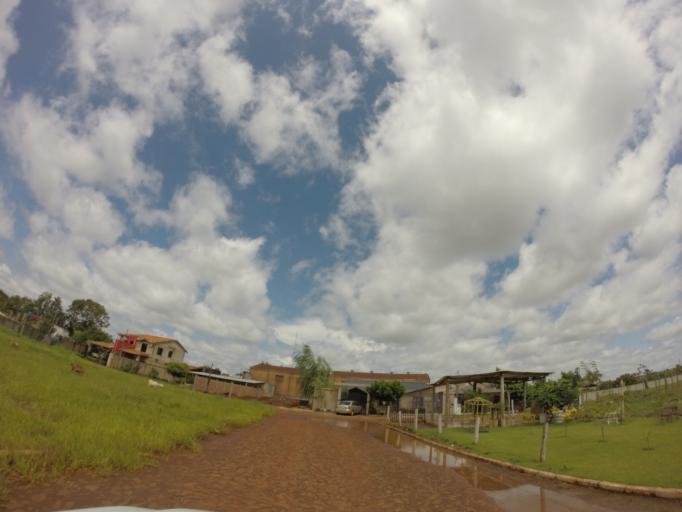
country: PY
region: Alto Parana
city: Ciudad del Este
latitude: -25.4062
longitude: -54.6367
